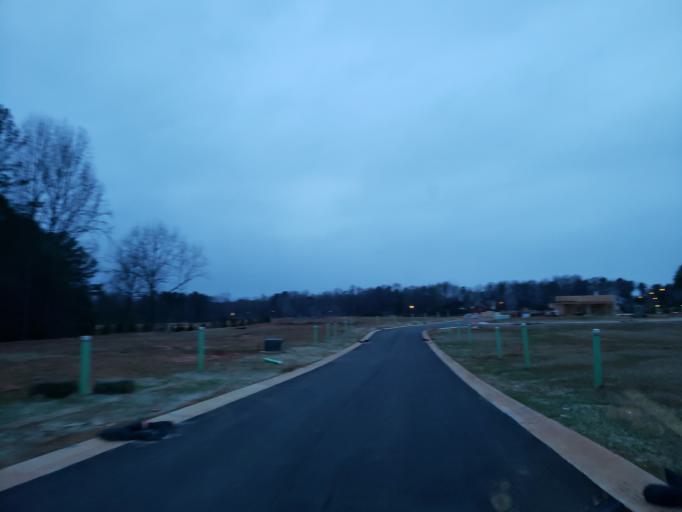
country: US
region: Georgia
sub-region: Cobb County
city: Mableton
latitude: 33.8398
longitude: -84.5788
